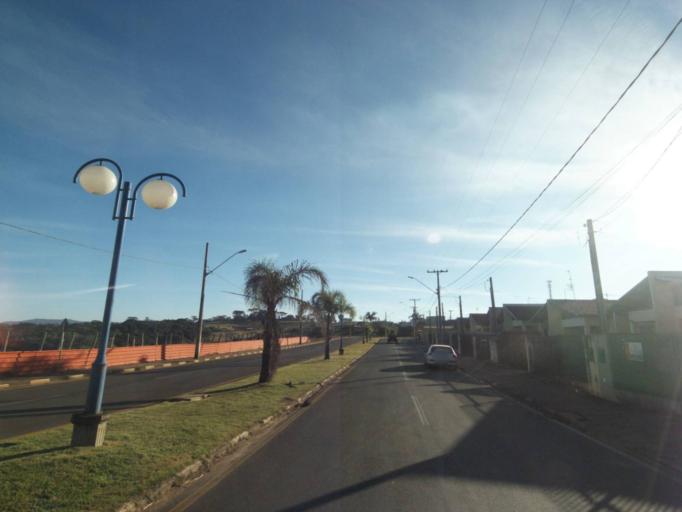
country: BR
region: Parana
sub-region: Tibagi
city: Tibagi
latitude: -24.5244
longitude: -50.4058
